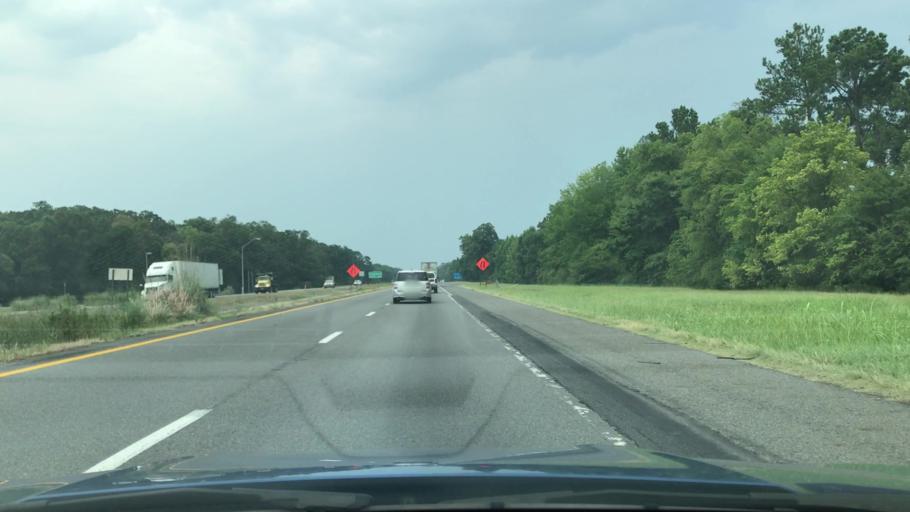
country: US
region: Texas
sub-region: Harrison County
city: Waskom
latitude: 32.4622
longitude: -94.0453
